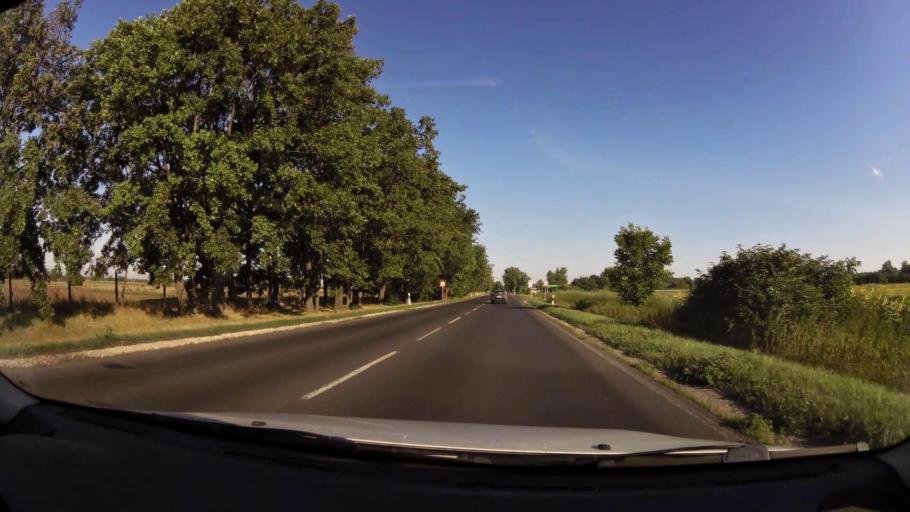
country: HU
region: Pest
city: Monor
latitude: 47.3178
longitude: 19.4787
